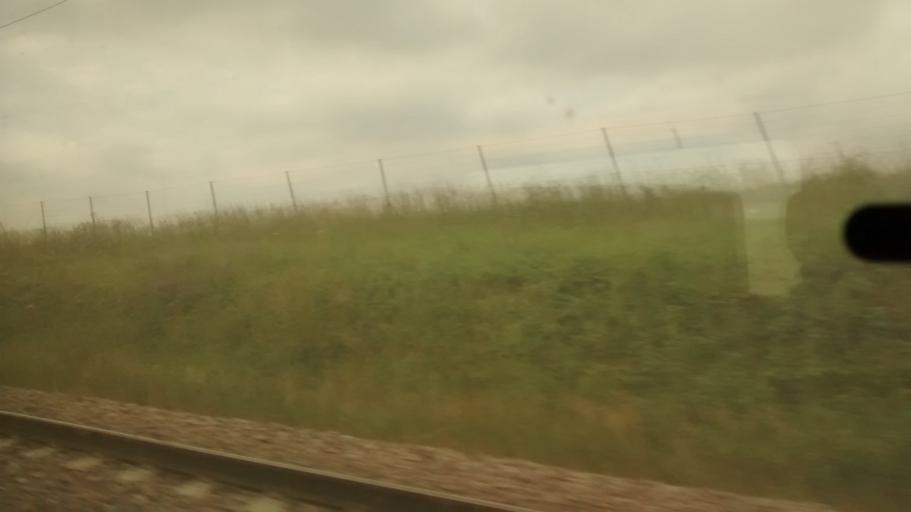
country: FR
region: Bourgogne
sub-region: Departement de l'Yonne
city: Ancy-le-Franc
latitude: 47.6382
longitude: 4.1069
